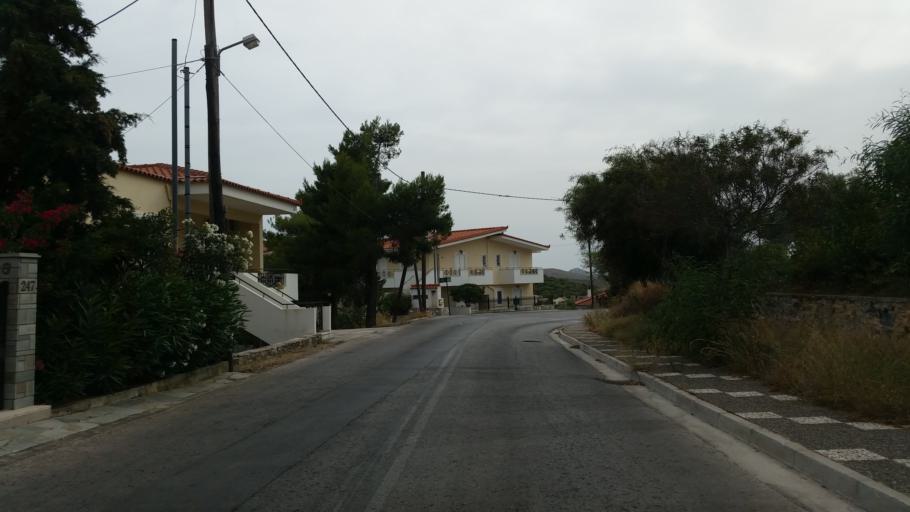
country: GR
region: Attica
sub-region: Nomarchia Anatolikis Attikis
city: Lavrio
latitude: 37.7243
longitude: 24.0172
